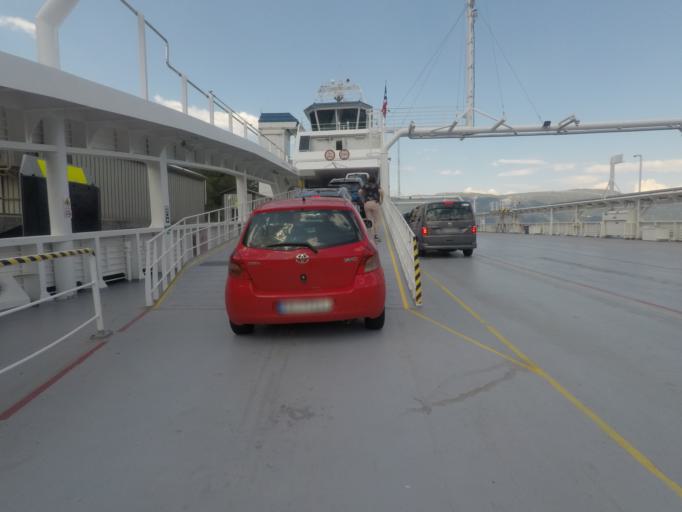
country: NO
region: Sogn og Fjordane
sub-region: Hyllestad
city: Hyllestad
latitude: 61.0548
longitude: 5.5040
